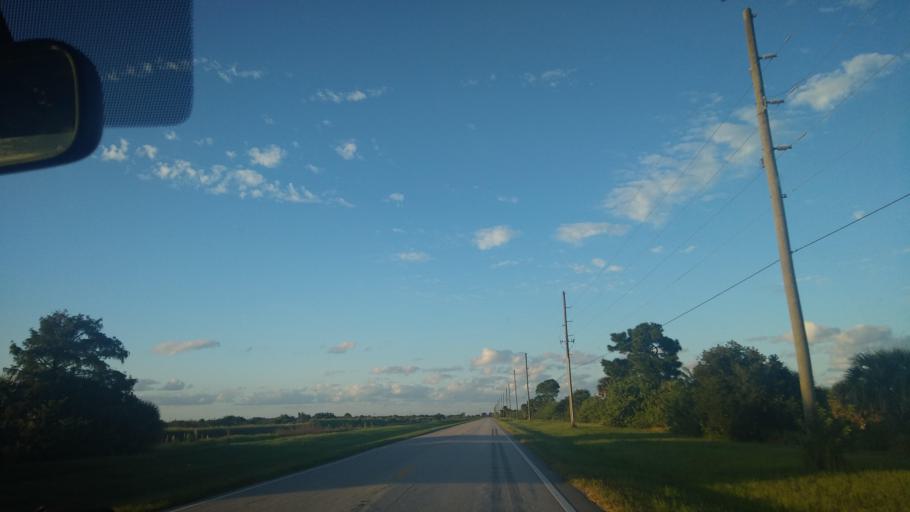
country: US
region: Florida
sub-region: Indian River County
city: Fellsmere
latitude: 27.7297
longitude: -80.6420
